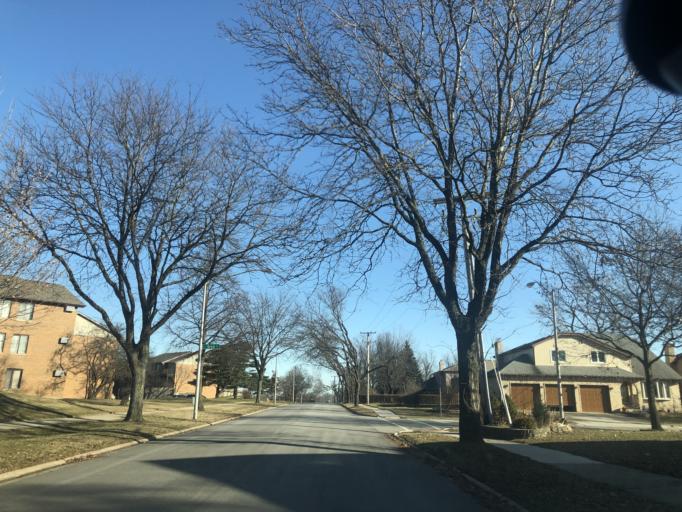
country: US
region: Illinois
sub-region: DuPage County
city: Addison
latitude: 41.9361
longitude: -88.0070
